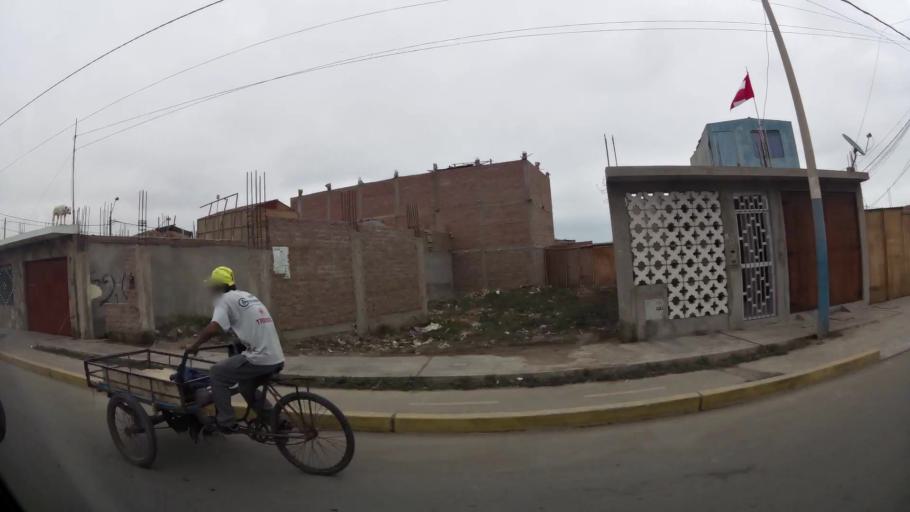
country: PE
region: Ica
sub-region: Provincia de Pisco
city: Pisco
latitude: -13.7126
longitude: -76.2103
